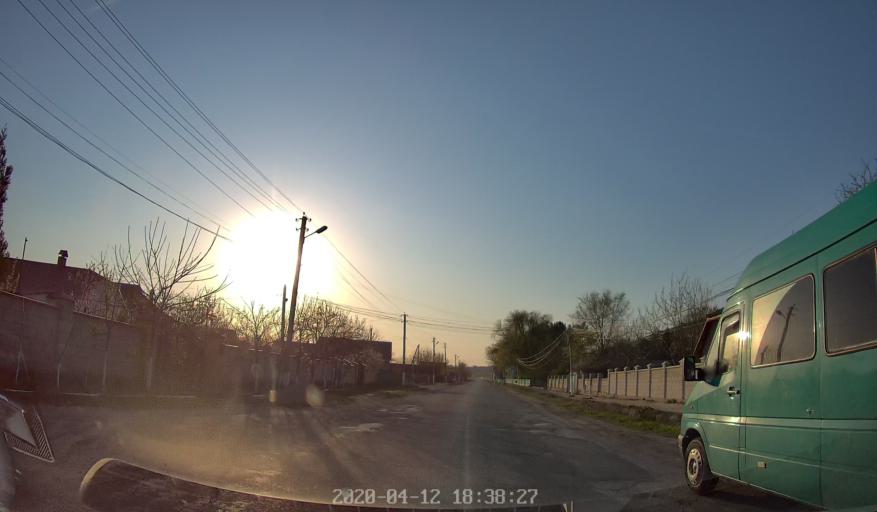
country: MD
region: Chisinau
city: Vadul lui Voda
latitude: 47.1243
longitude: 29.0006
